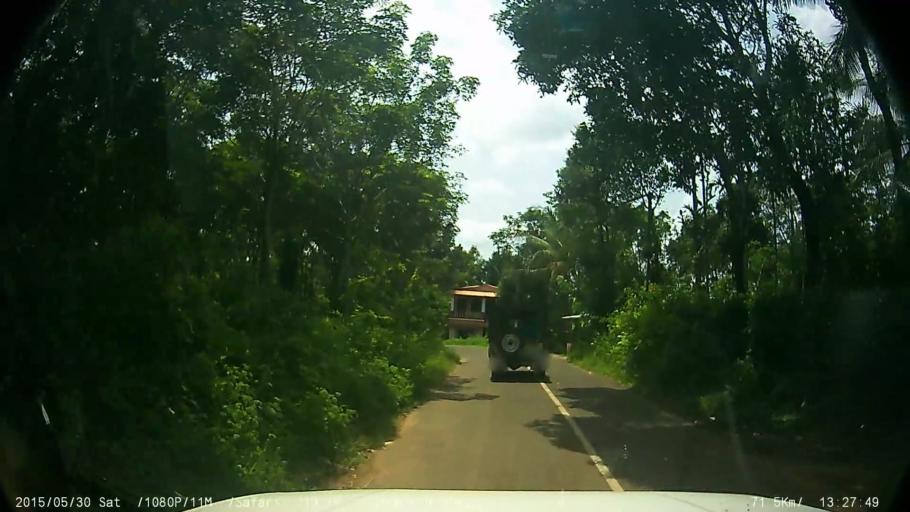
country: IN
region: Kerala
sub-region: Wayanad
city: Panamaram
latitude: 11.8227
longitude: 76.0869
